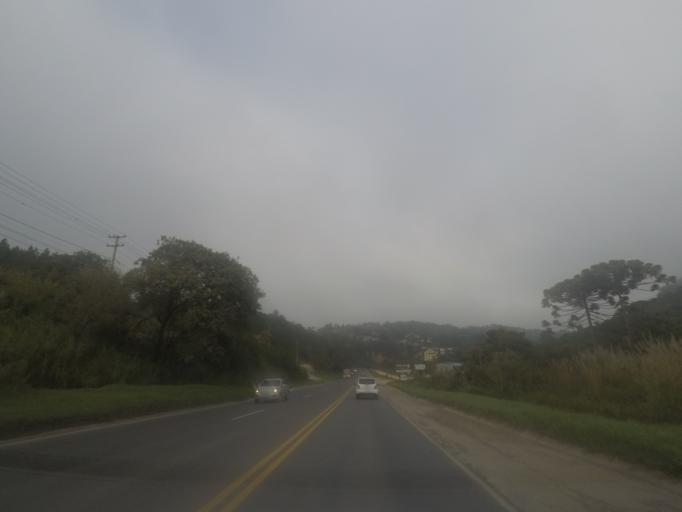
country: BR
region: Parana
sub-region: Almirante Tamandare
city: Almirante Tamandare
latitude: -25.2847
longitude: -49.3057
